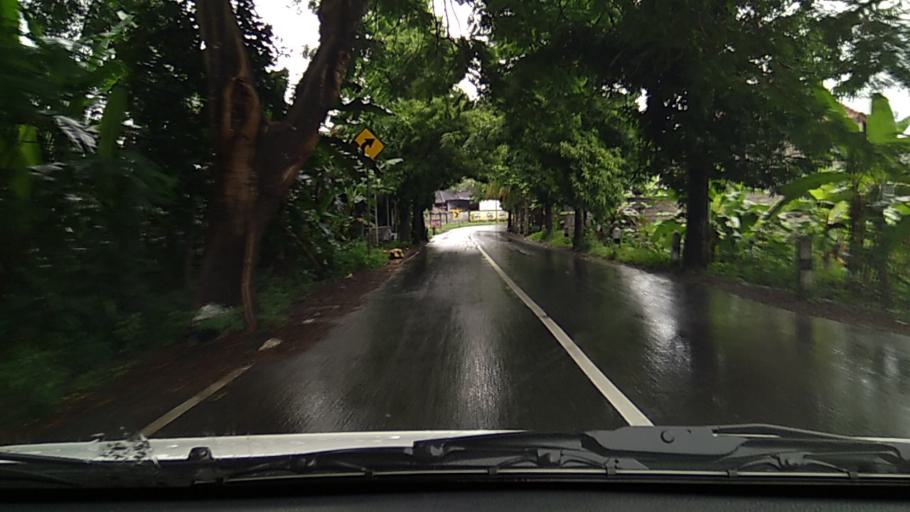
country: ID
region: Bali
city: Banjar Bugbug
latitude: -8.4934
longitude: 115.5879
